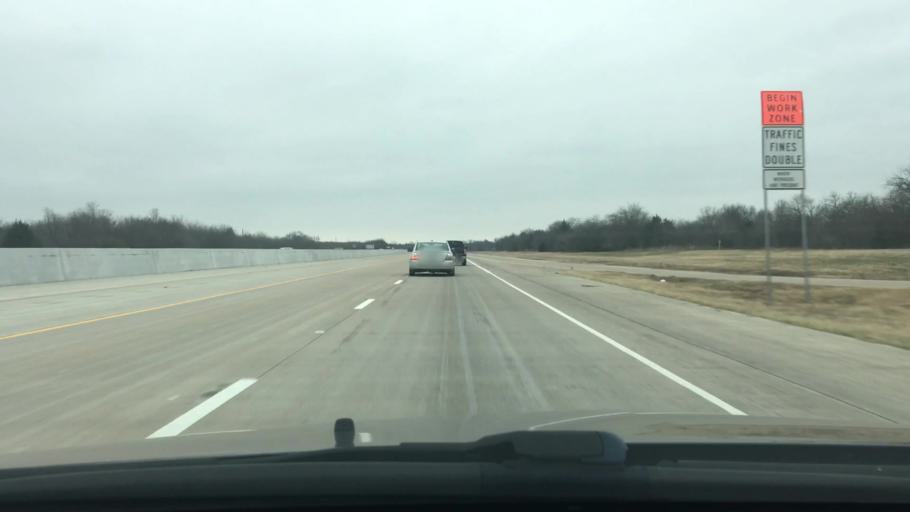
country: US
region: Texas
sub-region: Freestone County
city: Wortham
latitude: 31.8772
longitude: -96.3431
